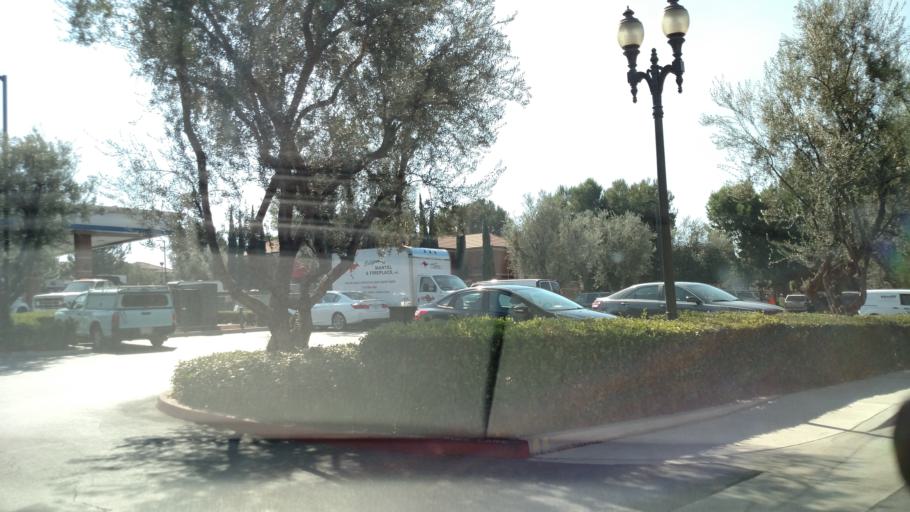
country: US
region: California
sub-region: Orange County
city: Lake Forest
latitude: 33.6958
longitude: -117.7418
